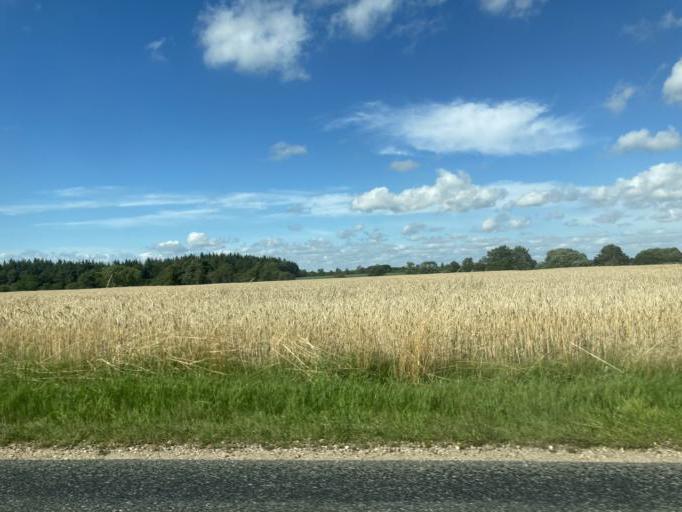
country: DK
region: South Denmark
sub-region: Esbjerg Kommune
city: Ribe
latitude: 55.2859
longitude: 8.7139
